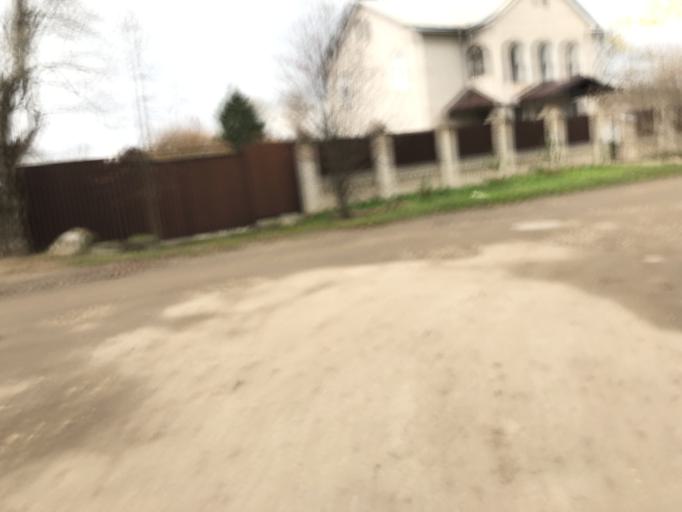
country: RU
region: Tverskaya
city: Rzhev
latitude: 56.2507
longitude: 34.3241
